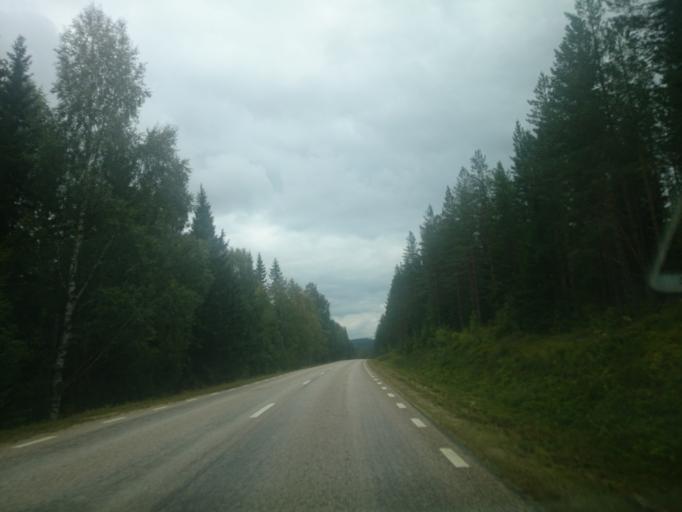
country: SE
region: Jaemtland
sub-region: Harjedalens Kommun
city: Sveg
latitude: 61.9794
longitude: 15.1075
